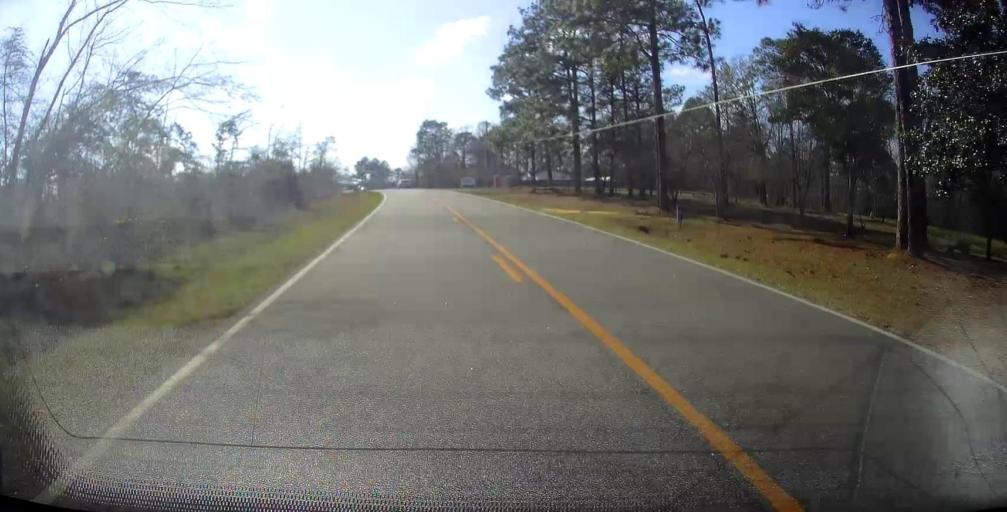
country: US
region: Georgia
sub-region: Laurens County
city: Dublin
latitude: 32.5357
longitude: -82.9670
